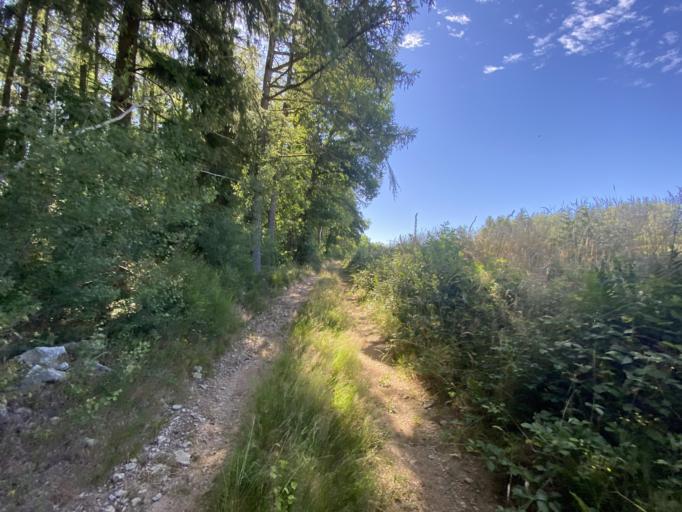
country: FR
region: Bourgogne
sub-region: Departement de la Cote-d'Or
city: Saulieu
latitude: 47.2915
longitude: 4.1277
